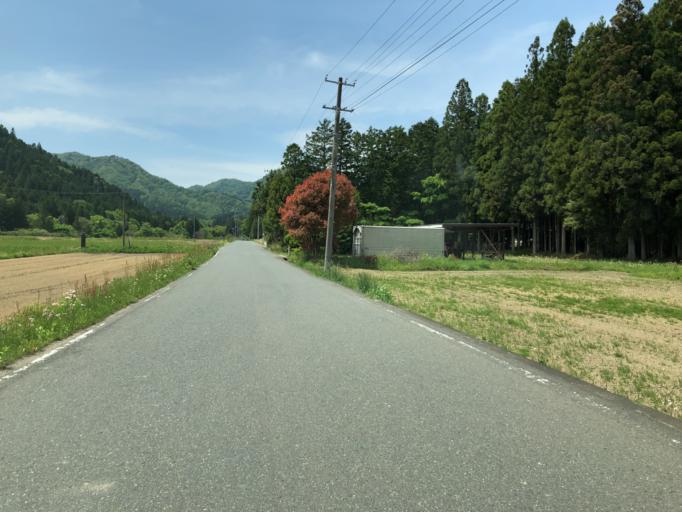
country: JP
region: Fukushima
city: Namie
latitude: 37.6891
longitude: 140.9029
